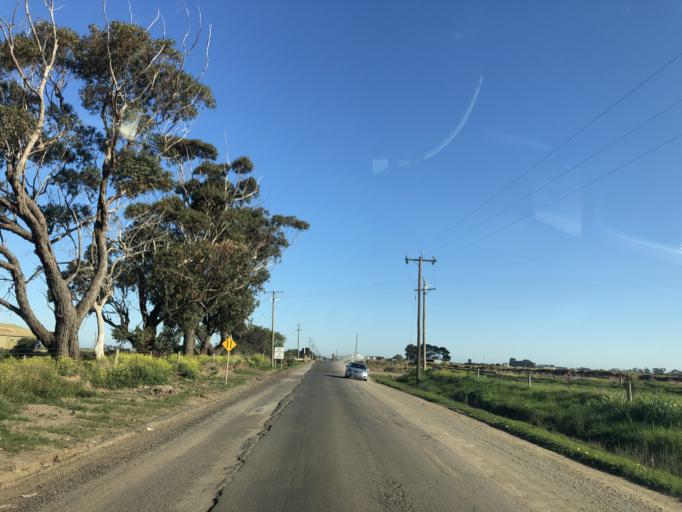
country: AU
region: Victoria
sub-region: Wyndham
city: Hoppers Crossing
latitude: -37.9130
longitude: 144.7007
